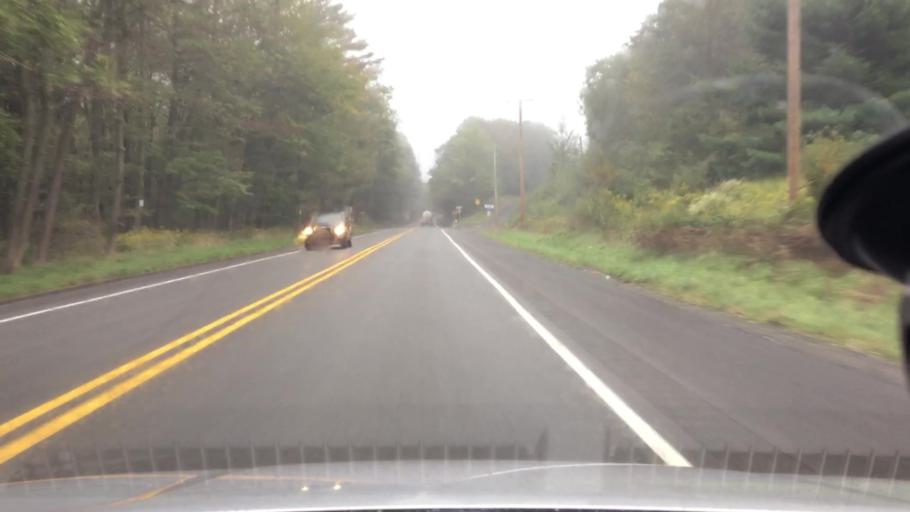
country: US
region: Pennsylvania
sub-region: Monroe County
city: Mount Pocono
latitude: 41.1270
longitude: -75.3443
